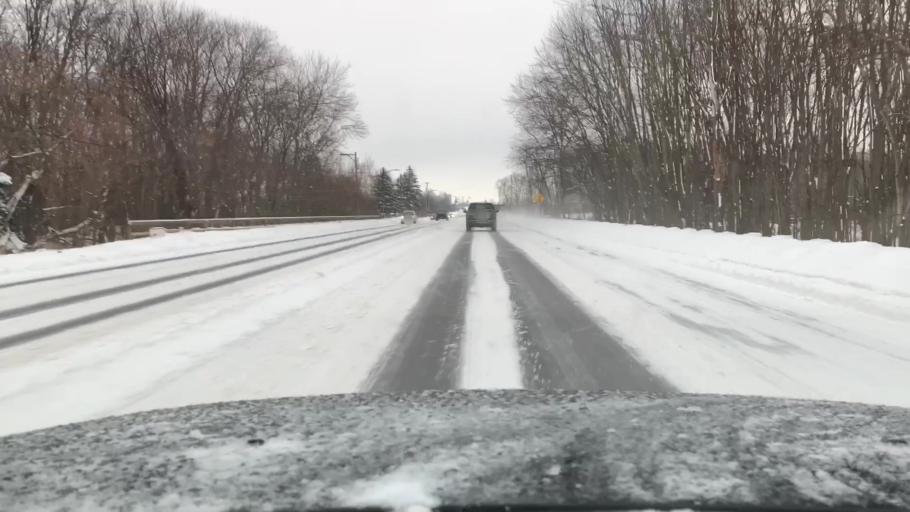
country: US
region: Michigan
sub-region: Ottawa County
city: Zeeland
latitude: 42.7830
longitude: -86.0394
